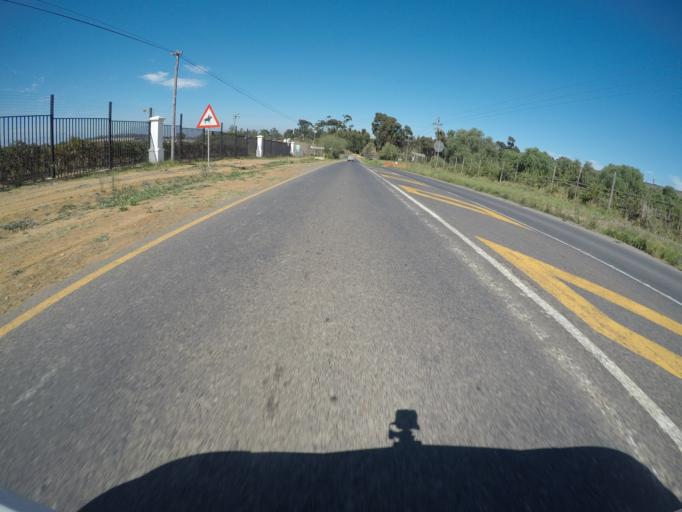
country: ZA
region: Western Cape
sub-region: City of Cape Town
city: Kraaifontein
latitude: -33.8089
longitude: 18.6248
